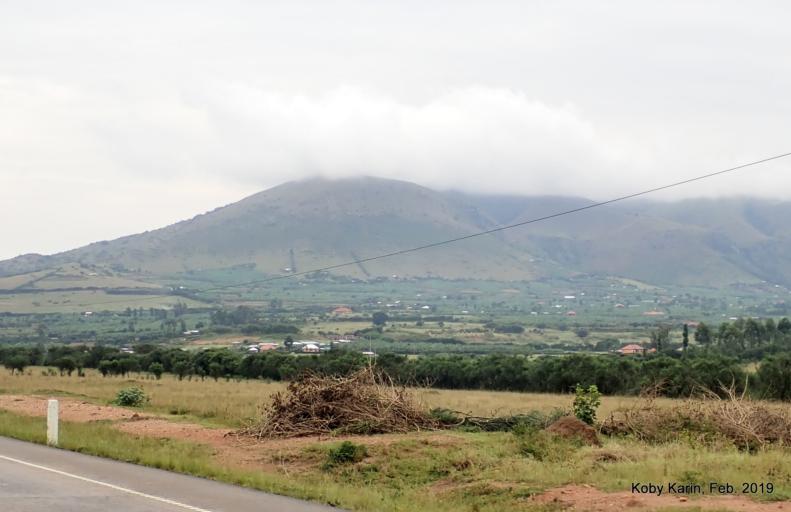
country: UG
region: Western Region
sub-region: Ntungamo District
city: Ntungamo
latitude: -1.0894
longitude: 30.1817
